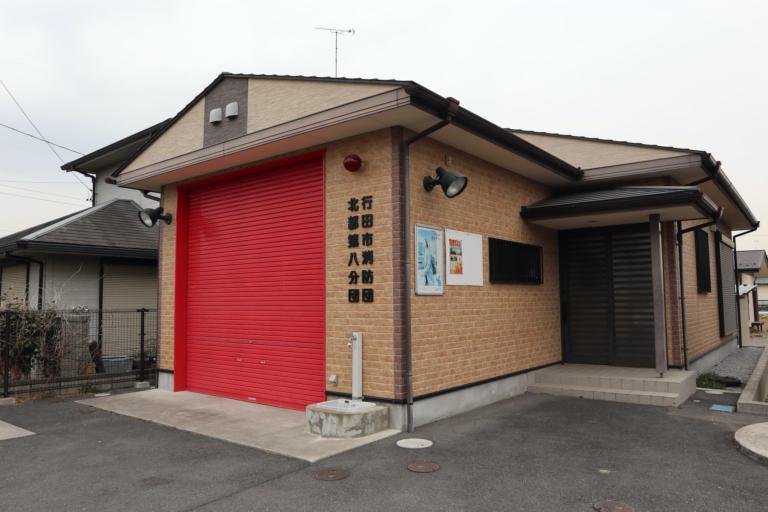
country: JP
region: Saitama
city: Gyoda
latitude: 36.1657
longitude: 139.4856
